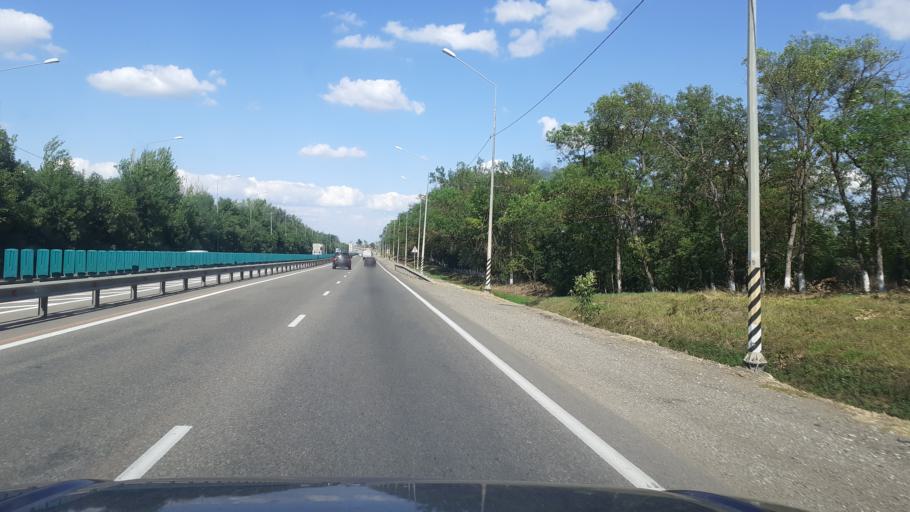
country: RU
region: Krasnodarskiy
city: Severskaya
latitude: 44.8343
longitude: 38.6822
